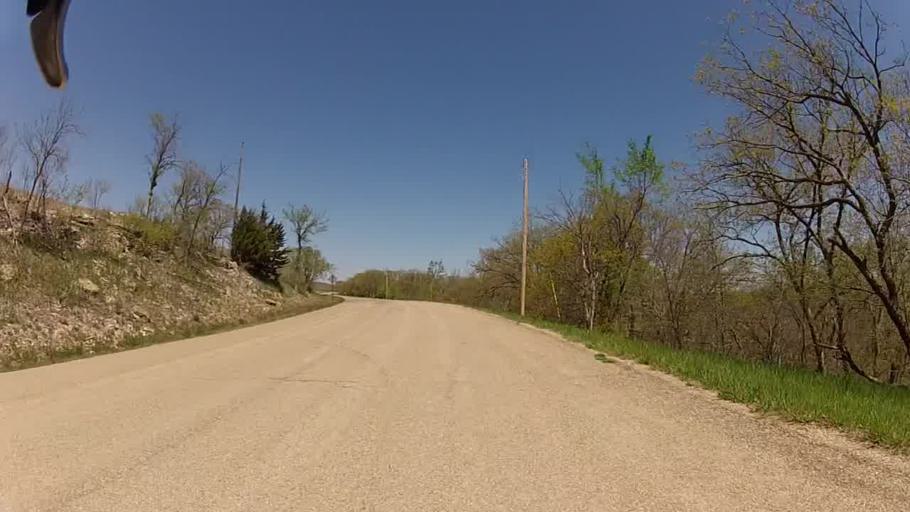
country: US
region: Kansas
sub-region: Riley County
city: Ogden
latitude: 38.9999
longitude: -96.5979
